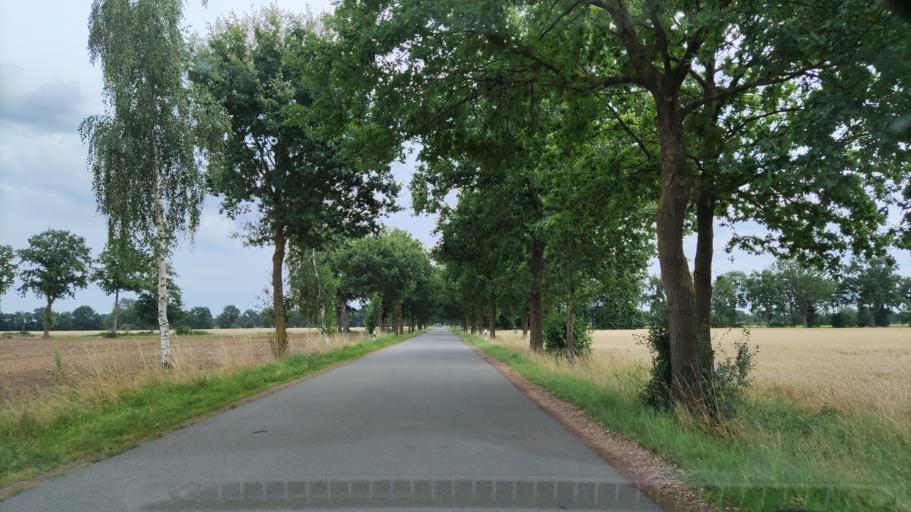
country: DE
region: Lower Saxony
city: Dannenberg
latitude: 53.0853
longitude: 11.1317
